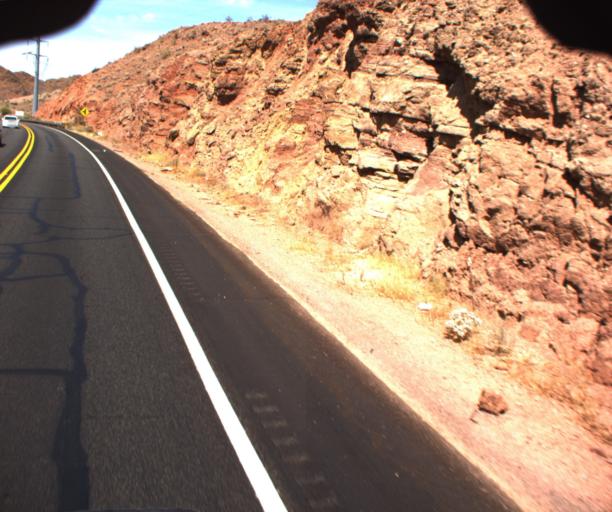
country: US
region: Arizona
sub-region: La Paz County
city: Cienega Springs
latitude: 34.2757
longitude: -114.1307
